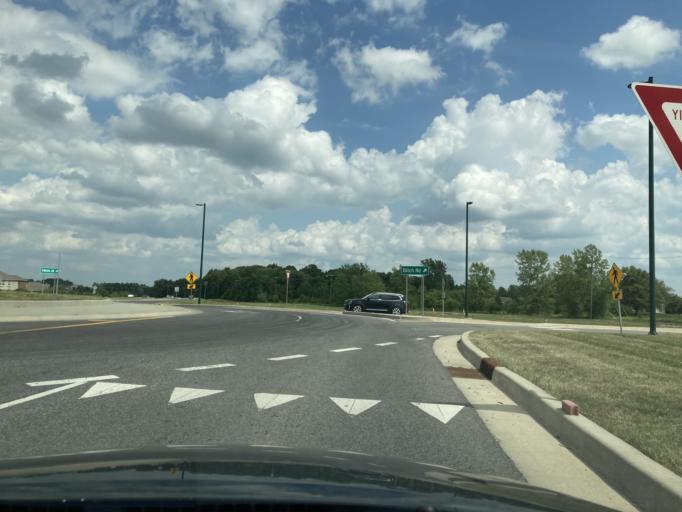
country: US
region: Indiana
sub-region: Hamilton County
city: Carmel
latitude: 40.0000
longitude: -86.1840
